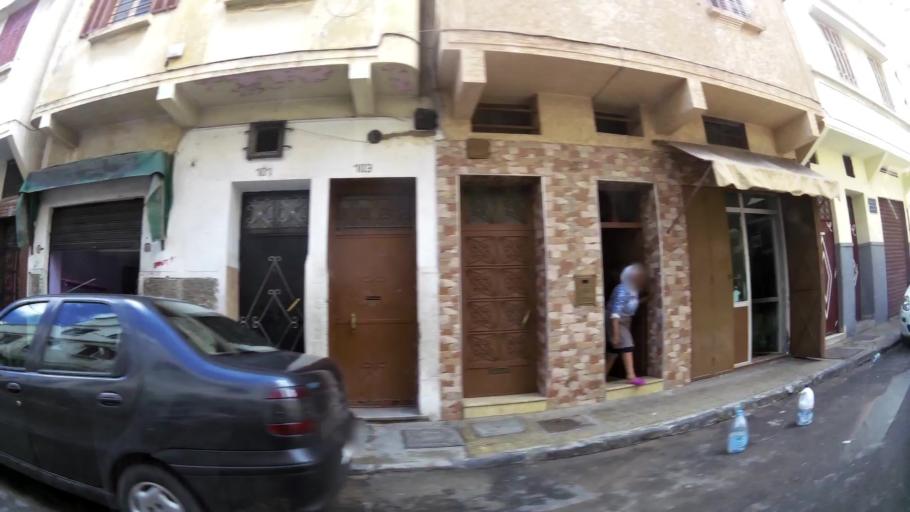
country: MA
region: Grand Casablanca
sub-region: Casablanca
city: Casablanca
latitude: 33.5599
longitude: -7.6014
